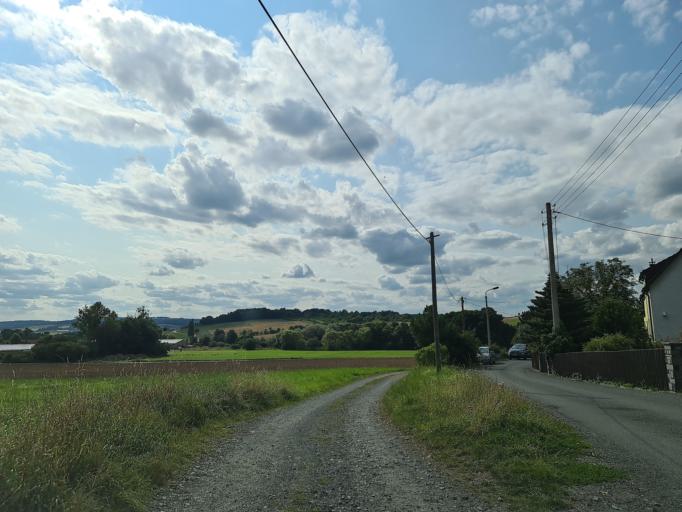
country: DE
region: Saxony
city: Weischlitz
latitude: 50.4927
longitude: 12.0806
